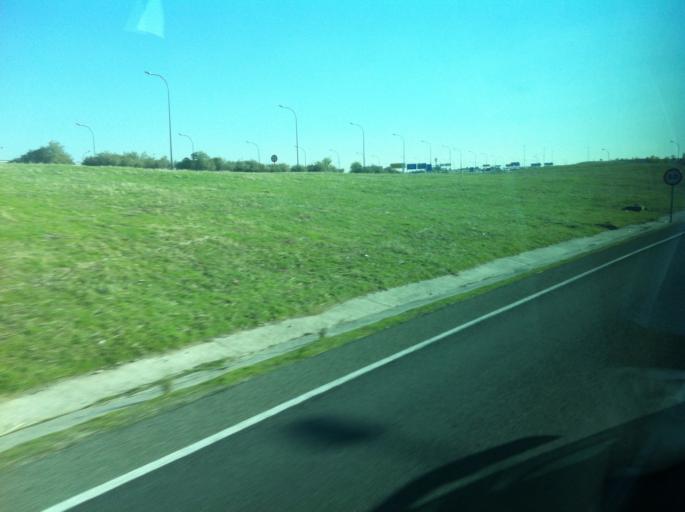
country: ES
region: Madrid
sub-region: Provincia de Madrid
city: Barajas de Madrid
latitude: 40.4897
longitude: -3.6030
